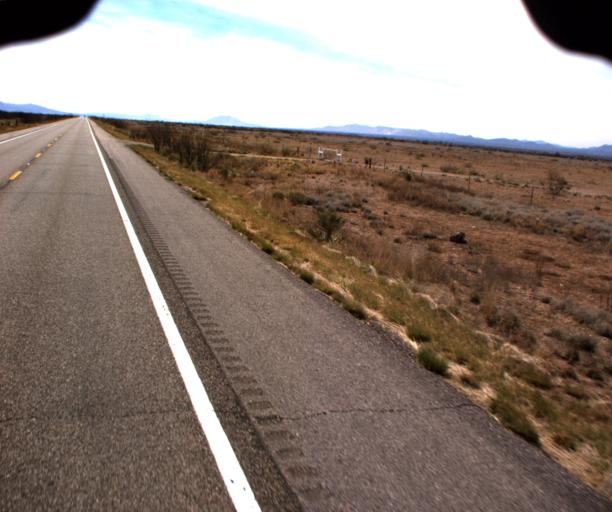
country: US
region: Arizona
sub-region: Cochise County
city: Pirtleville
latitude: 31.4958
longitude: -109.6327
